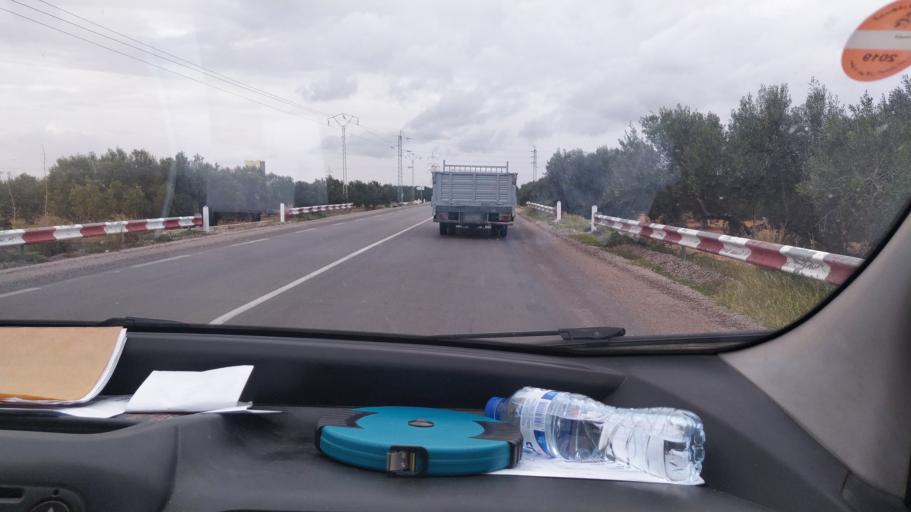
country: TN
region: Al Munastir
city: Sidi Bin Nur
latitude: 35.4836
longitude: 10.9445
